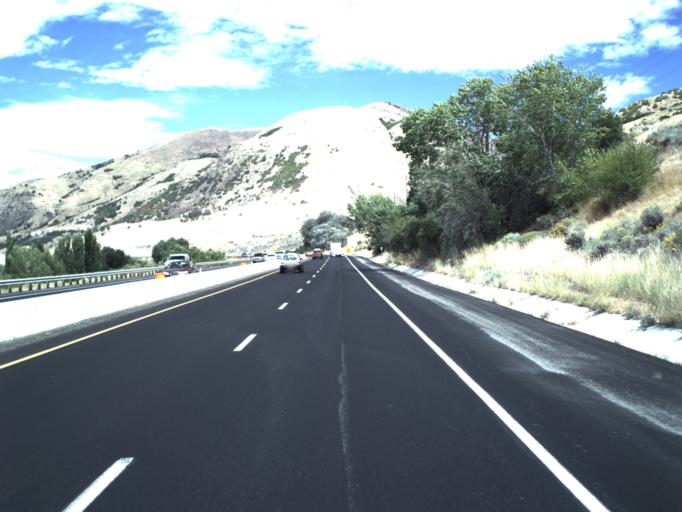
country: US
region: Utah
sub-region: Box Elder County
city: Brigham City
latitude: 41.4904
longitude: -112.0005
